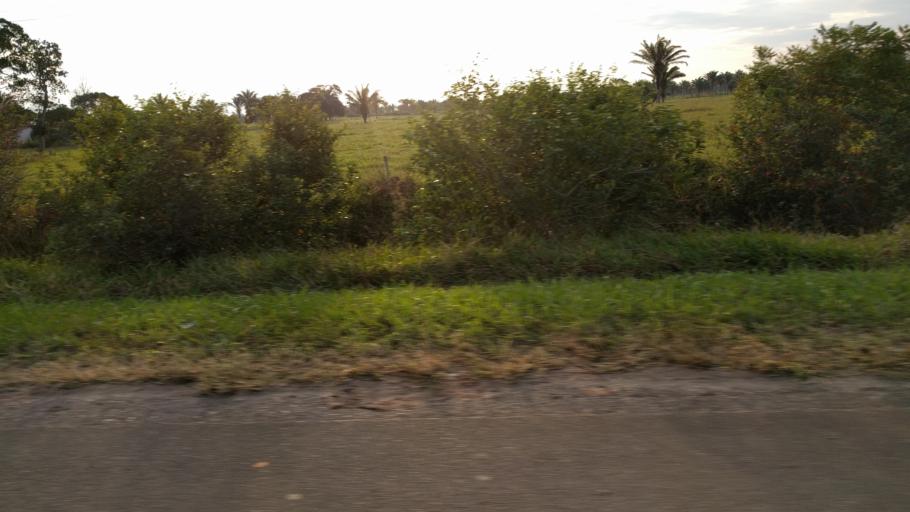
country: BO
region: Santa Cruz
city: Buena Vista
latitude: -17.4220
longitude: -63.6242
